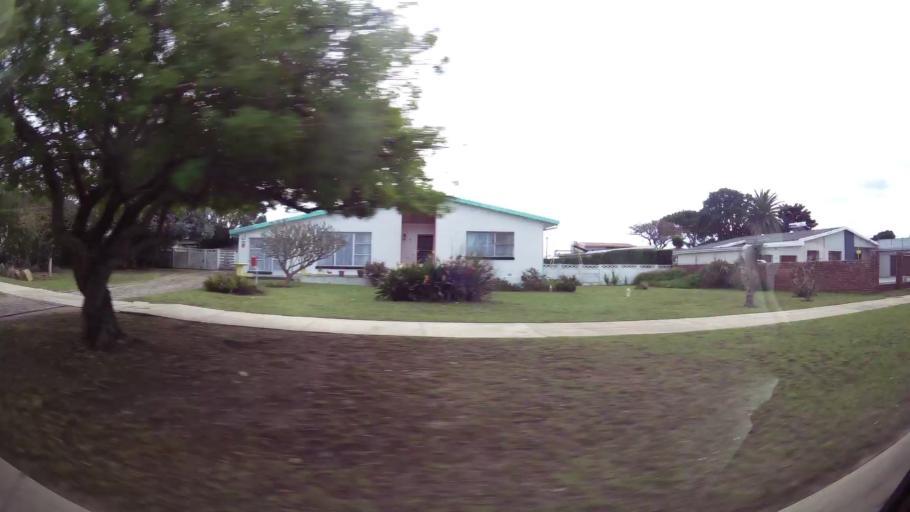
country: ZA
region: Eastern Cape
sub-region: Nelson Mandela Bay Metropolitan Municipality
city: Port Elizabeth
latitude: -33.9357
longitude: 25.5245
